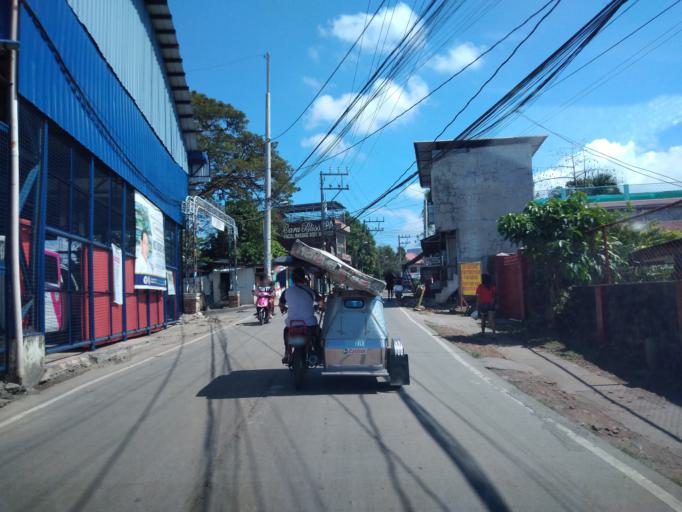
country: PH
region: Central Luzon
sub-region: Province of Bulacan
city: Bitungol
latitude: 14.8594
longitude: 121.0500
